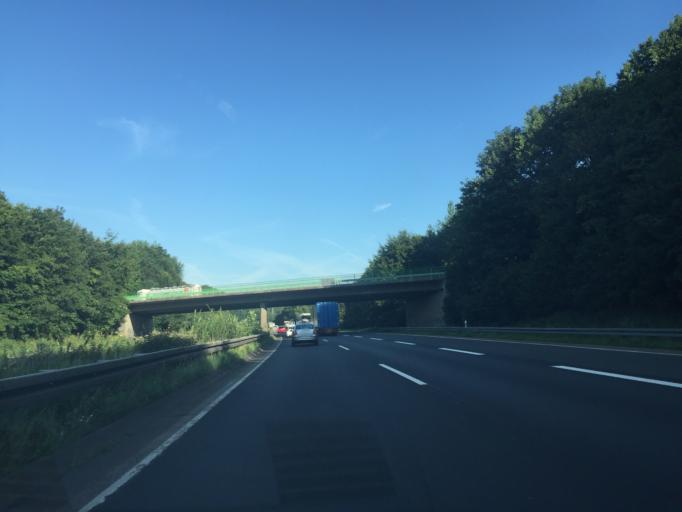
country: DE
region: North Rhine-Westphalia
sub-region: Regierungsbezirk Arnsberg
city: Luedenscheid
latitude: 51.2315
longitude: 7.6601
